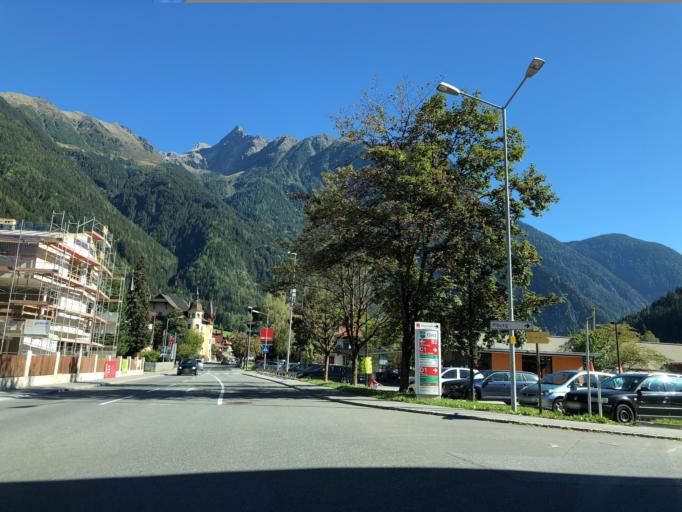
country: AT
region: Tyrol
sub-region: Politischer Bezirk Imst
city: Oetz
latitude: 47.2041
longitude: 10.8925
